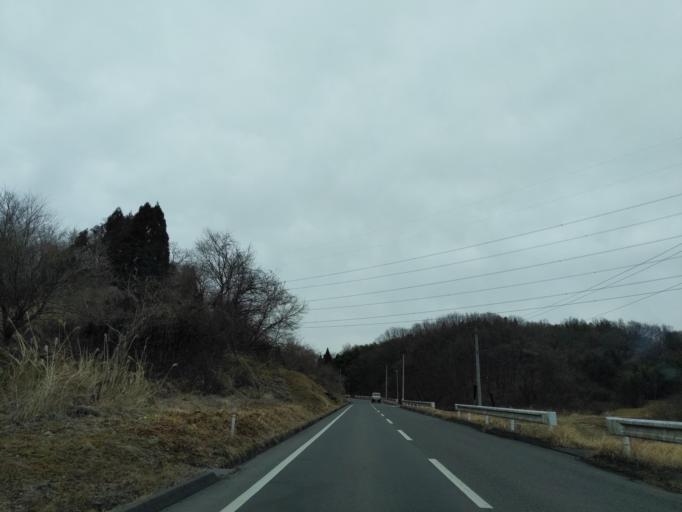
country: JP
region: Fukushima
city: Miharu
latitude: 37.4657
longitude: 140.4508
